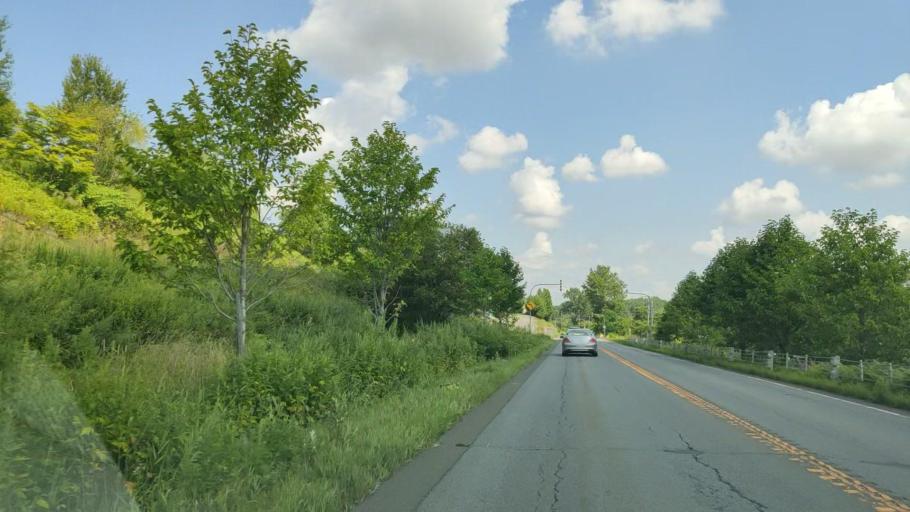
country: JP
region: Hokkaido
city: Shimo-furano
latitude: 43.5583
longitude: 142.4348
